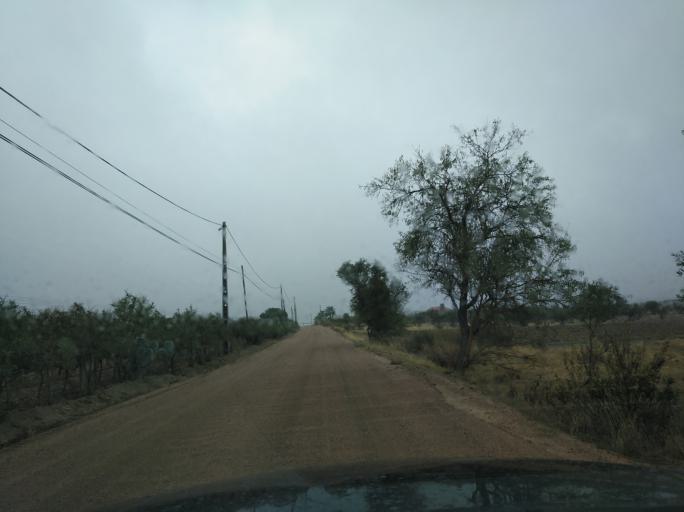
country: PT
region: Portalegre
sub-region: Campo Maior
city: Campo Maior
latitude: 38.9570
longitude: -7.0715
